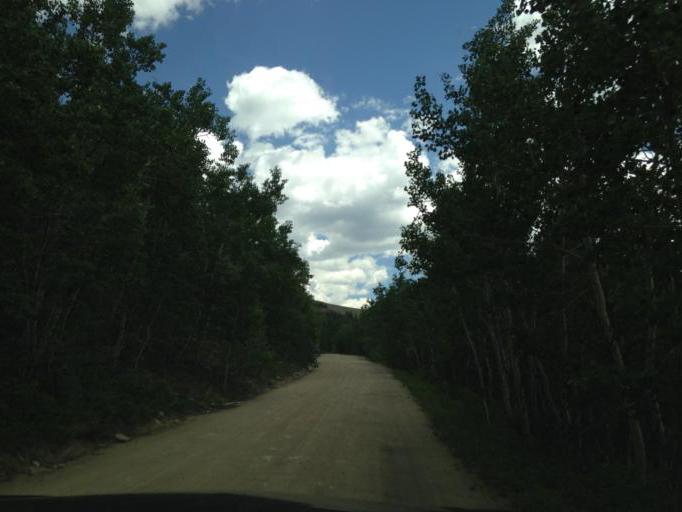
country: US
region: Colorado
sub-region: Park County
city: Fairplay
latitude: 39.3494
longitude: -105.9168
